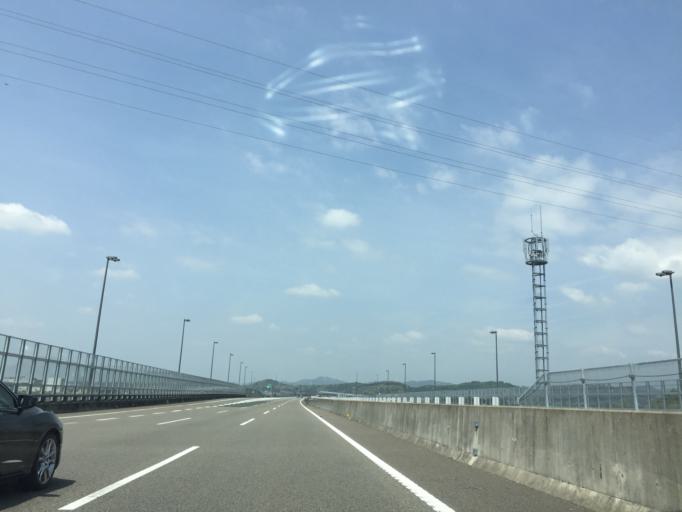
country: JP
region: Shizuoka
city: Hamakita
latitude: 34.8335
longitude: 137.8211
